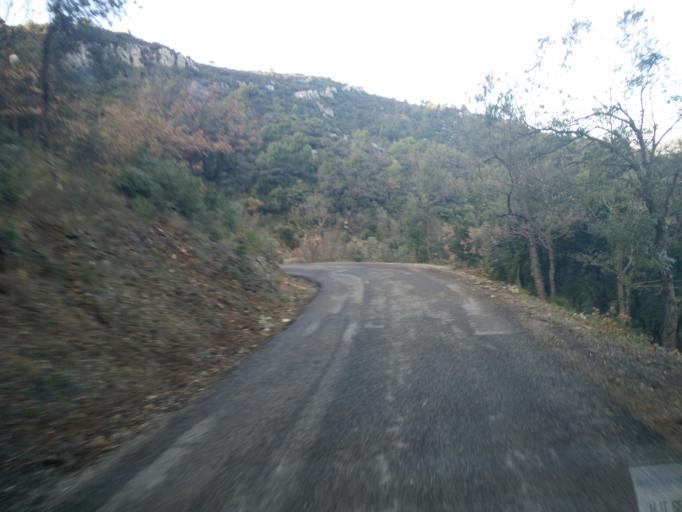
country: FR
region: Provence-Alpes-Cote d'Azur
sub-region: Departement du Var
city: Signes
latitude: 43.2674
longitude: 5.8468
